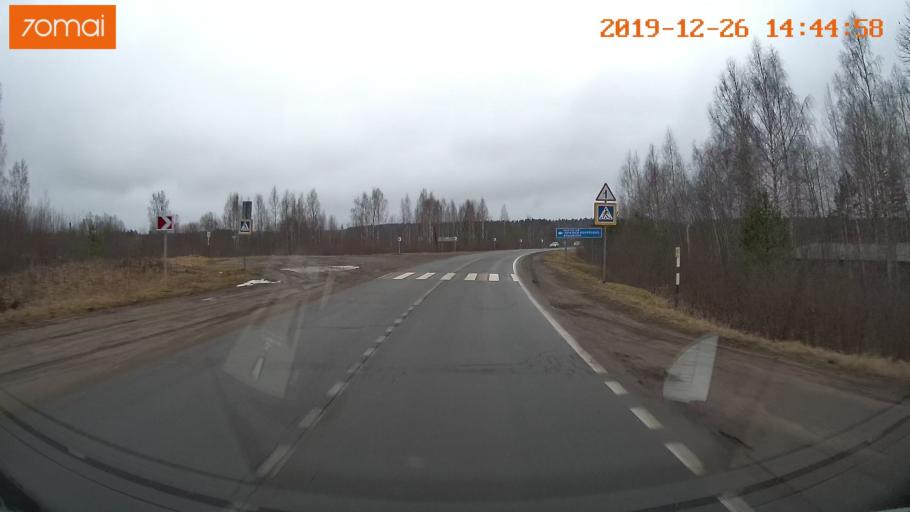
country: RU
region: Jaroslavl
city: Poshekhon'ye
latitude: 58.3414
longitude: 39.0490
